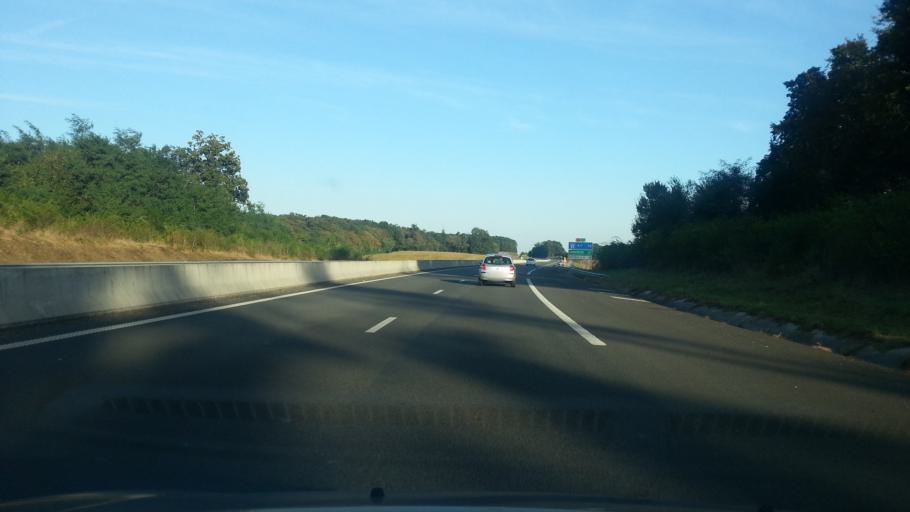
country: FR
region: Picardie
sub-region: Departement de l'Oise
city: Breuil-le-Sec
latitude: 49.3859
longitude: 2.4675
